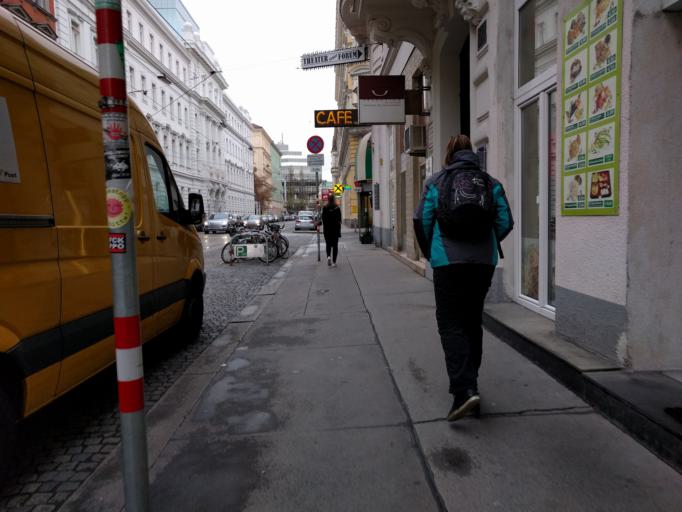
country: AT
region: Vienna
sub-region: Wien Stadt
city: Vienna
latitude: 48.2238
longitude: 16.3618
